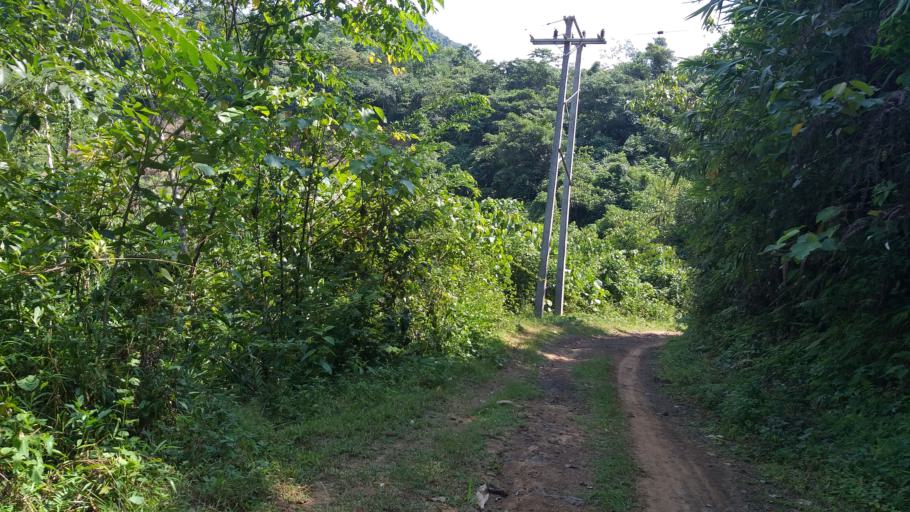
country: LA
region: Phongsali
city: Khoa
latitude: 21.3458
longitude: 102.5361
